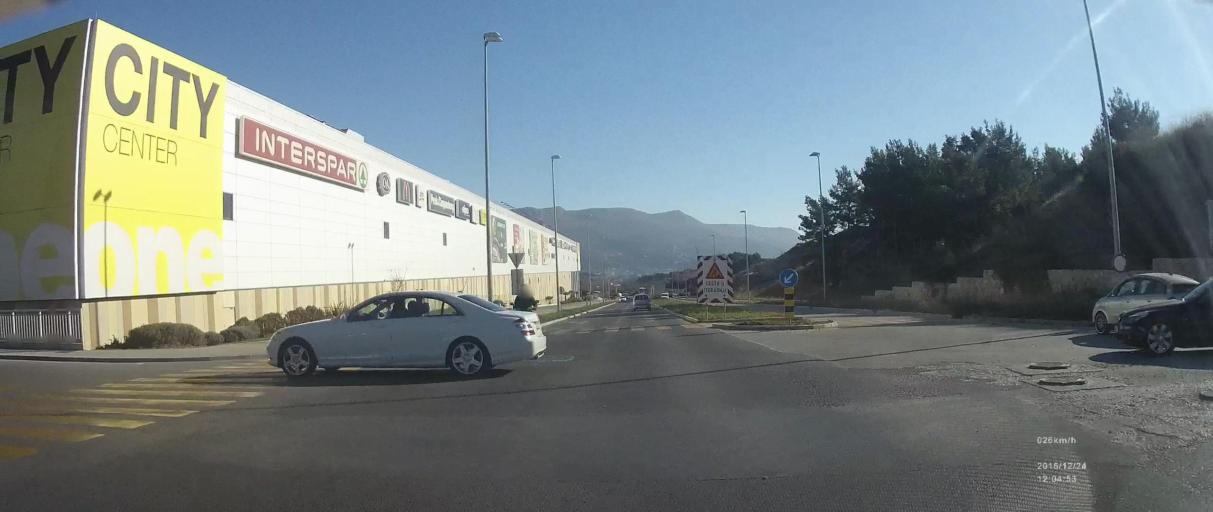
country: HR
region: Splitsko-Dalmatinska
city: Kamen
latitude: 43.5134
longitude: 16.5007
